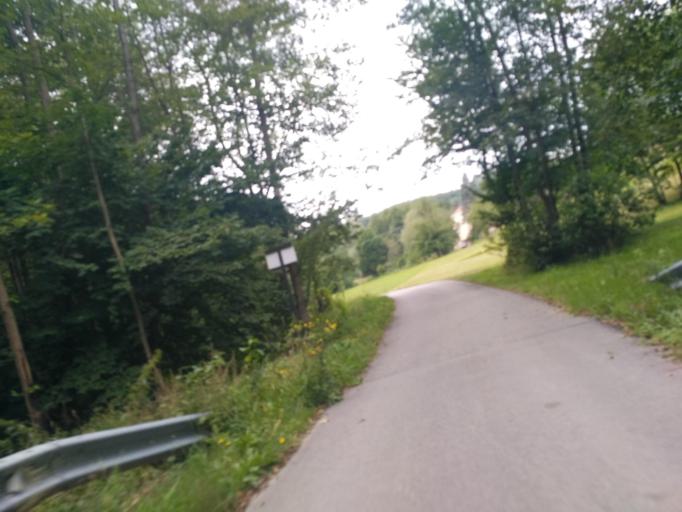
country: PL
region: Subcarpathian Voivodeship
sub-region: Powiat rzeszowski
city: Chmielnik
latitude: 49.9952
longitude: 22.1288
